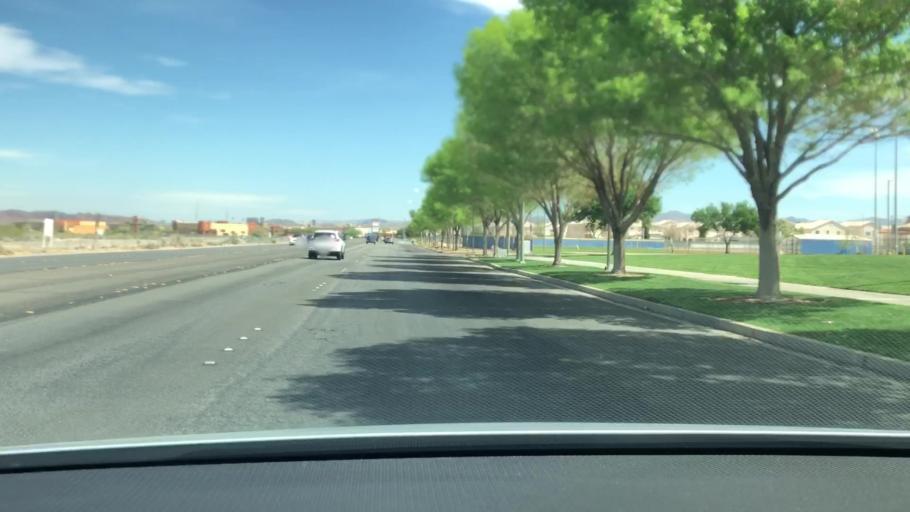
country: US
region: Nevada
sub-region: Clark County
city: Whitney
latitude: 36.0838
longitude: -115.0398
